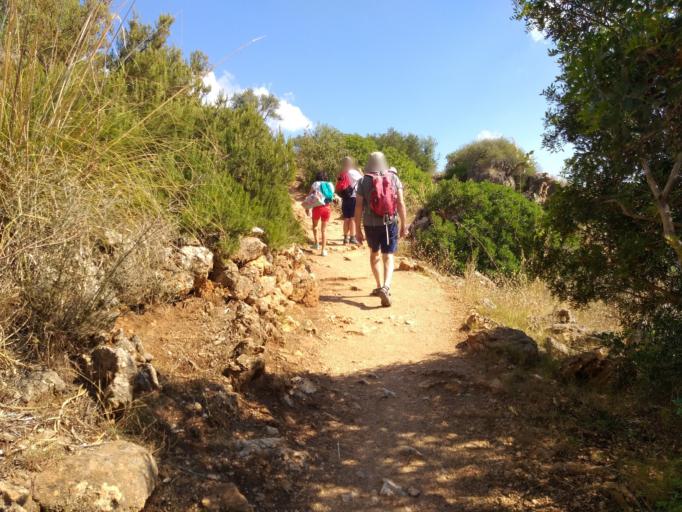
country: IT
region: Sicily
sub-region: Trapani
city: Castelluzzo
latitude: 38.0842
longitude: 12.8074
